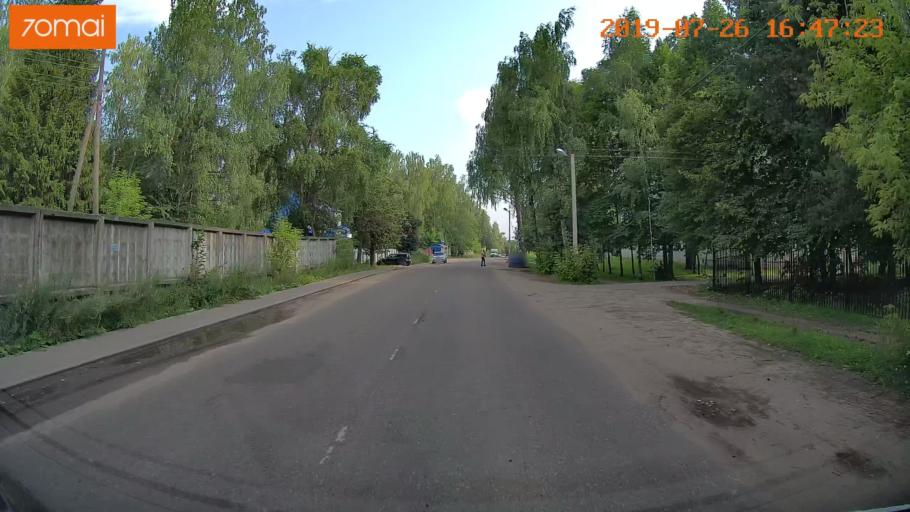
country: RU
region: Ivanovo
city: Bogorodskoye
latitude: 57.0418
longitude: 41.0119
